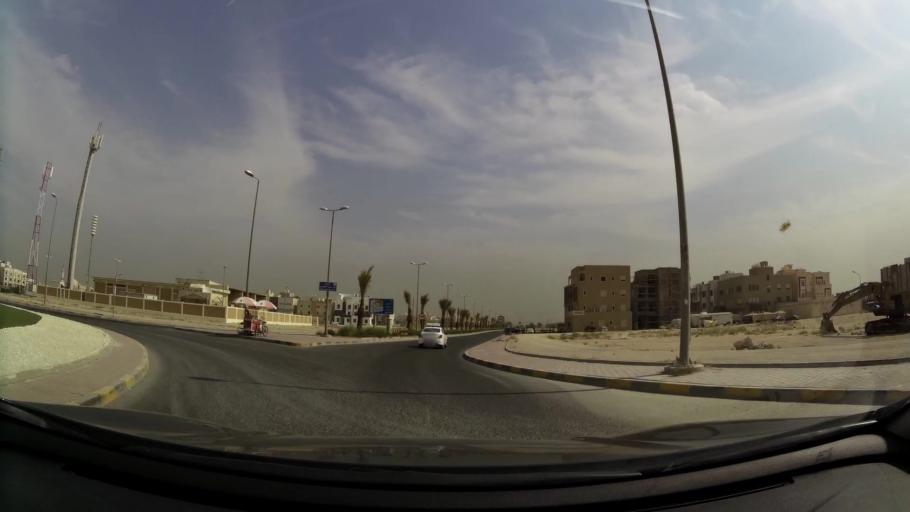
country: KW
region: Al Farwaniyah
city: Janub as Surrah
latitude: 29.2905
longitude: 47.9981
